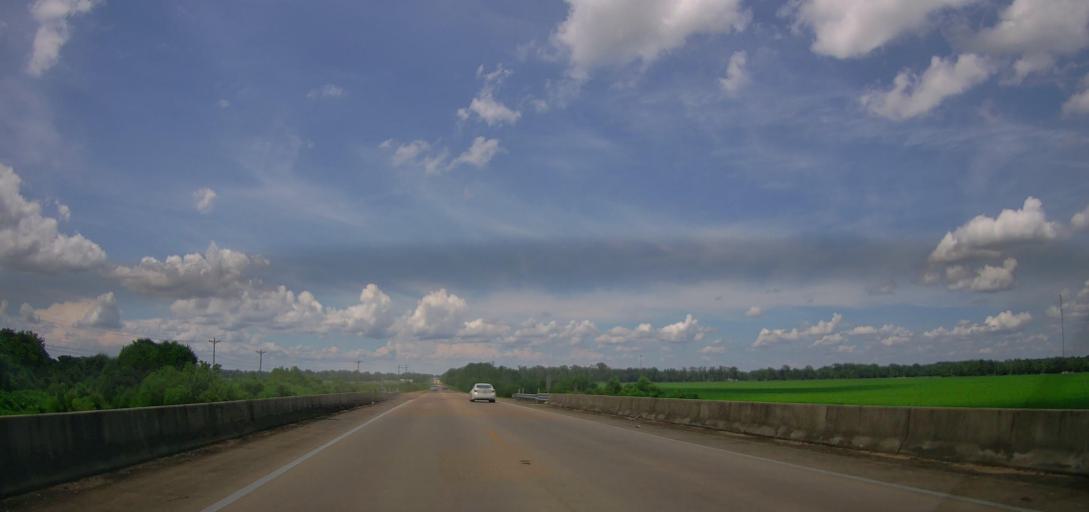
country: US
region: Mississippi
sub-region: Lee County
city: Shannon
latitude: 34.1383
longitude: -88.7193
